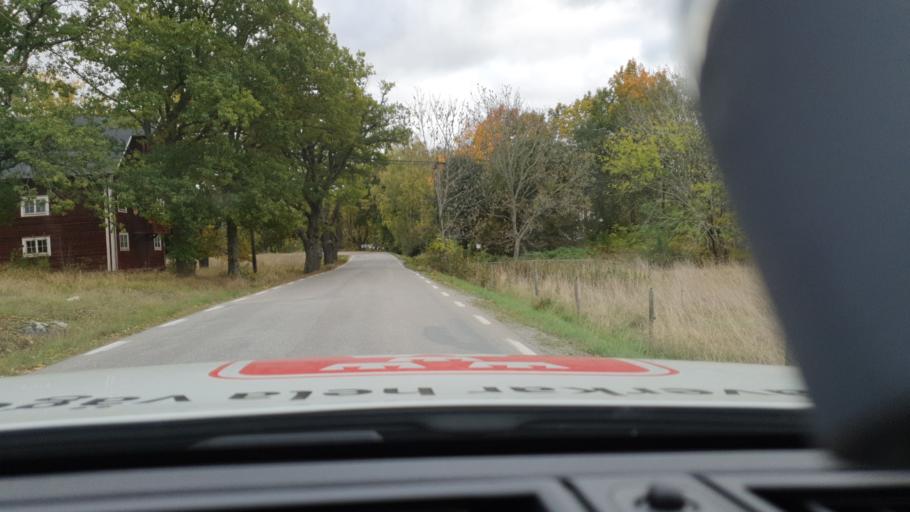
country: SE
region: Stockholm
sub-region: Upplands-Bro Kommun
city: Bro
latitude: 59.5047
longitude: 17.5740
